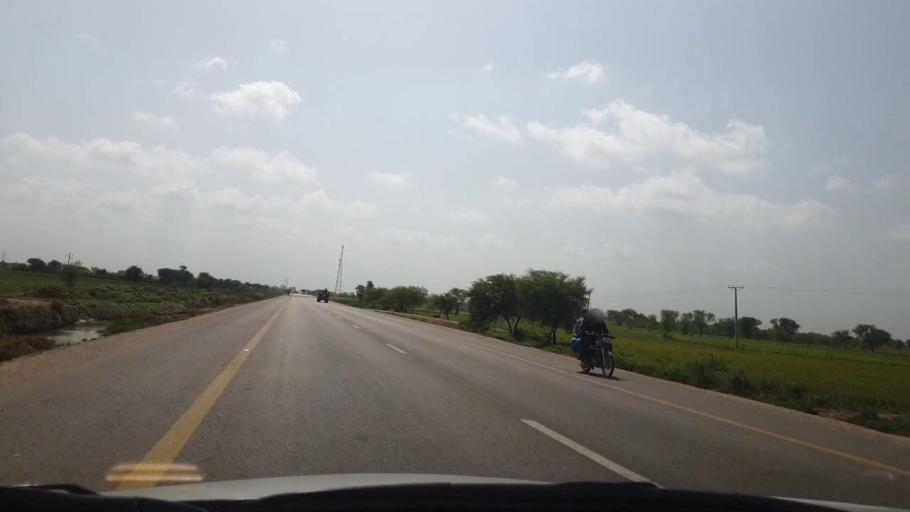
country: PK
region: Sindh
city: Matli
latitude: 24.9589
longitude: 68.6862
